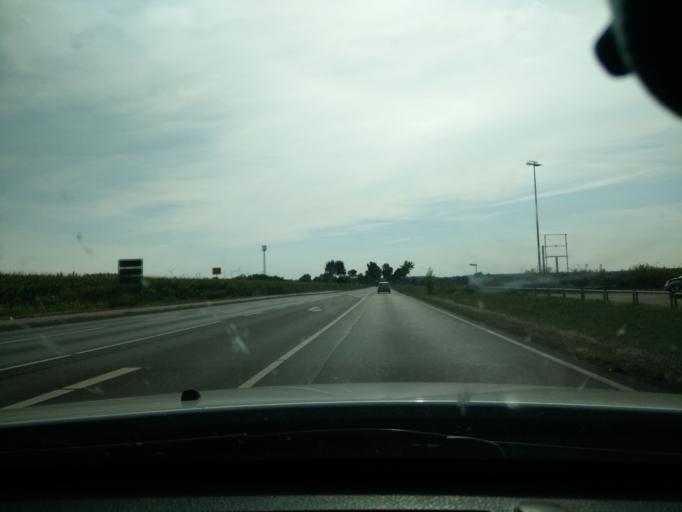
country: DE
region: Saxony-Anhalt
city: Burg bei Magdeburg
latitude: 52.2580
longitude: 11.8415
